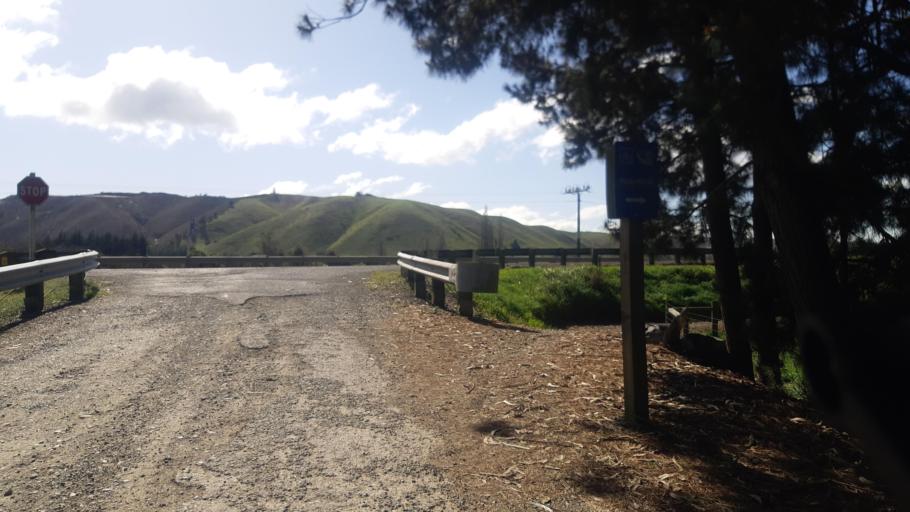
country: NZ
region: Tasman
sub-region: Tasman District
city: Wakefield
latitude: -41.4282
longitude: 172.9918
